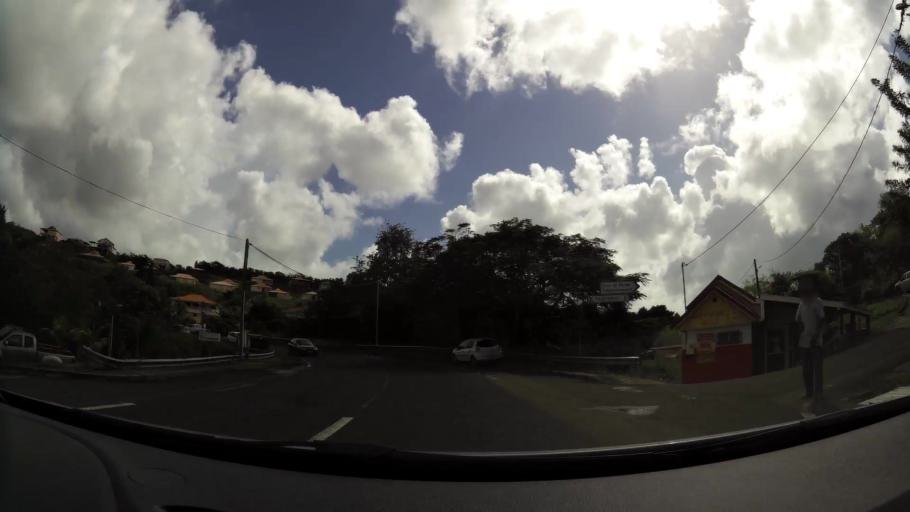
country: MQ
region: Martinique
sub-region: Martinique
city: Sainte-Luce
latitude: 14.4843
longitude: -60.9926
